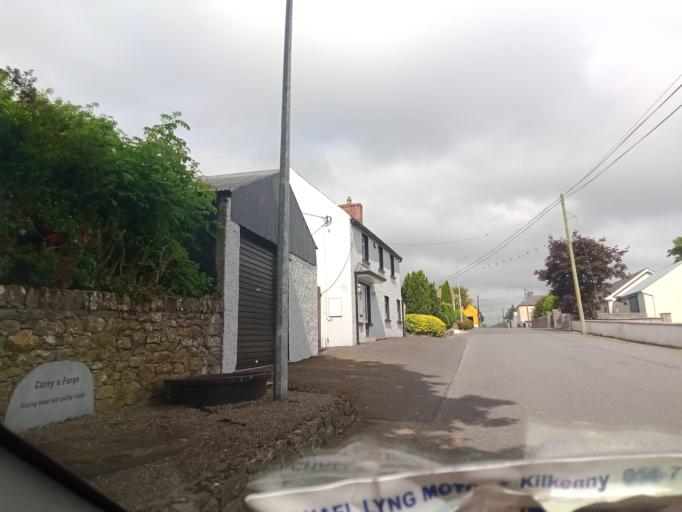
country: IE
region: Leinster
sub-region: Laois
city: Rathdowney
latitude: 52.7666
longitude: -7.4710
